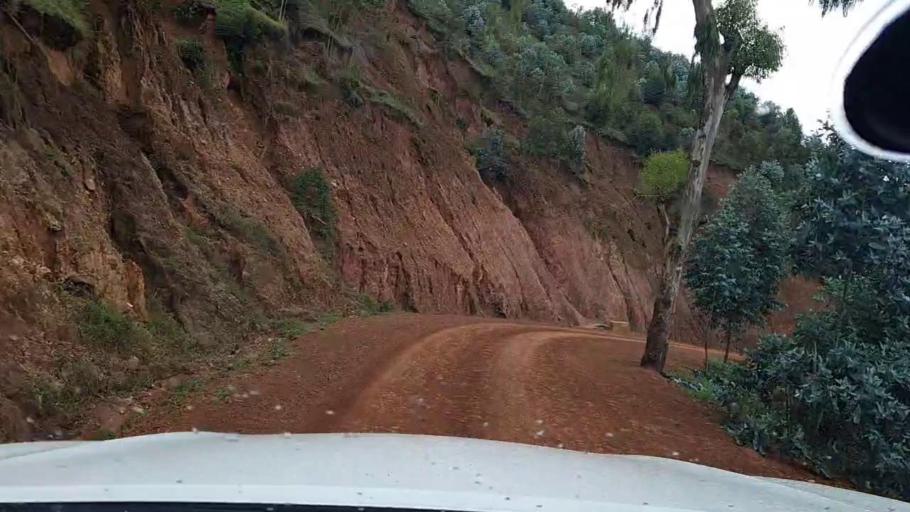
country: RW
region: Western Province
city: Kibuye
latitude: -2.1692
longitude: 29.4353
